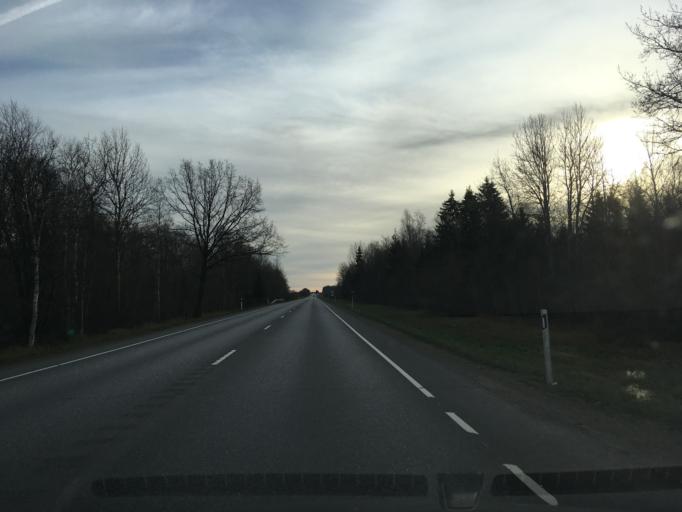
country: EE
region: Ida-Virumaa
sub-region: Kohtla-Jaerve linn
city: Kohtla-Jarve
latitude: 59.4164
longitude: 27.2927
